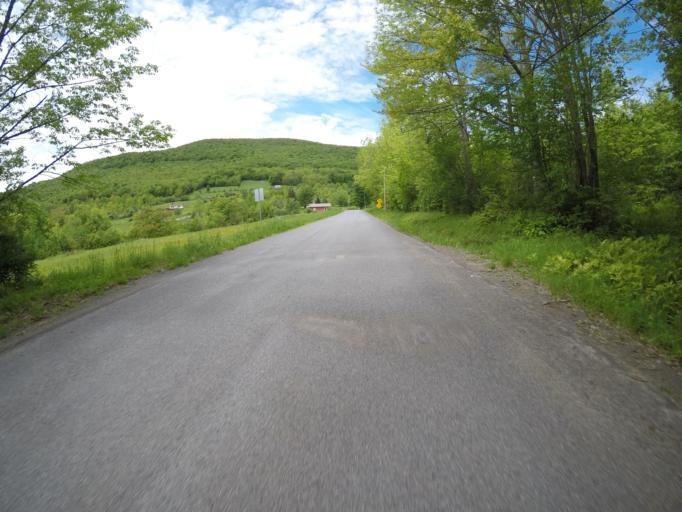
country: US
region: New York
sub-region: Delaware County
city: Stamford
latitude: 42.2810
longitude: -74.5139
